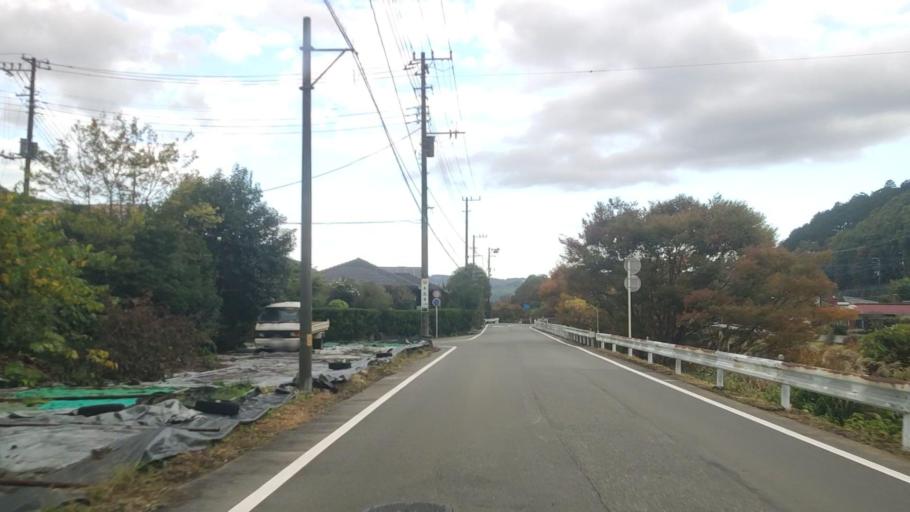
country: JP
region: Shizuoka
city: Ito
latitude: 34.9446
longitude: 138.9968
